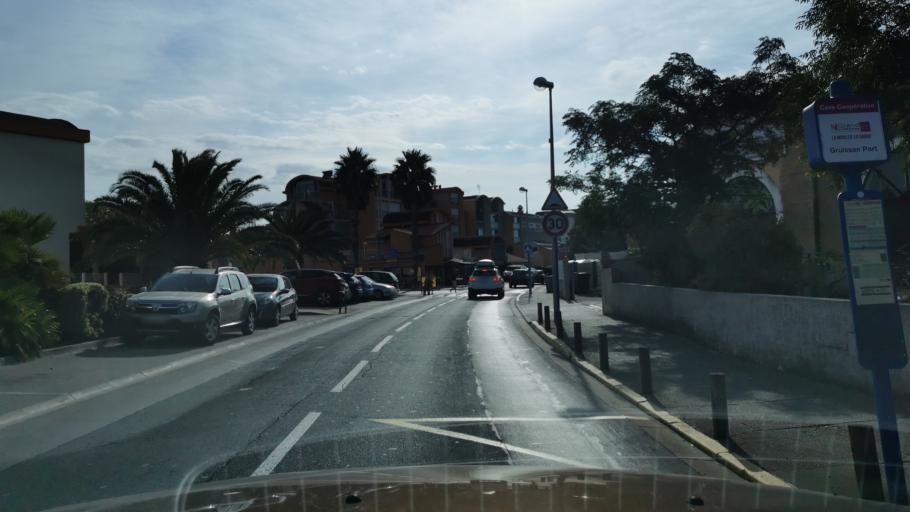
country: FR
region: Languedoc-Roussillon
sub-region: Departement de l'Aude
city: Gruissan
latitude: 43.1083
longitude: 3.0927
